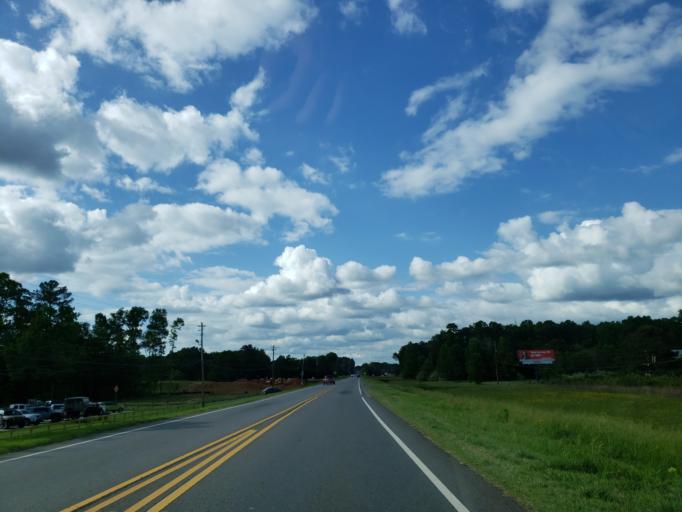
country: US
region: Georgia
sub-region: Bartow County
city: Cartersville
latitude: 34.2355
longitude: -84.8565
